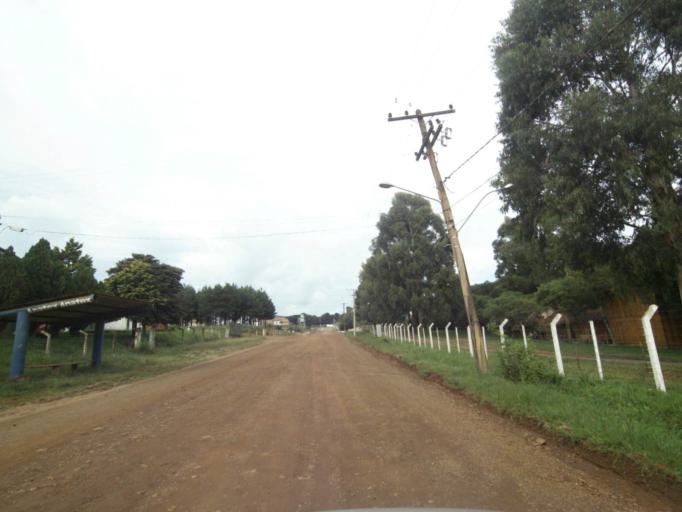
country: BR
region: Rio Grande do Sul
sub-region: Lagoa Vermelha
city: Lagoa Vermelha
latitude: -28.2331
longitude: -51.4967
